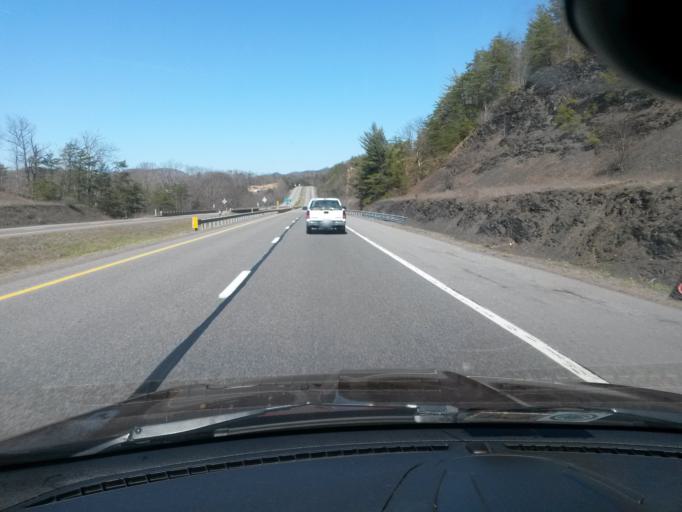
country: US
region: West Virginia
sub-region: Greenbrier County
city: White Sulphur Springs
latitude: 37.7896
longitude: -80.2951
